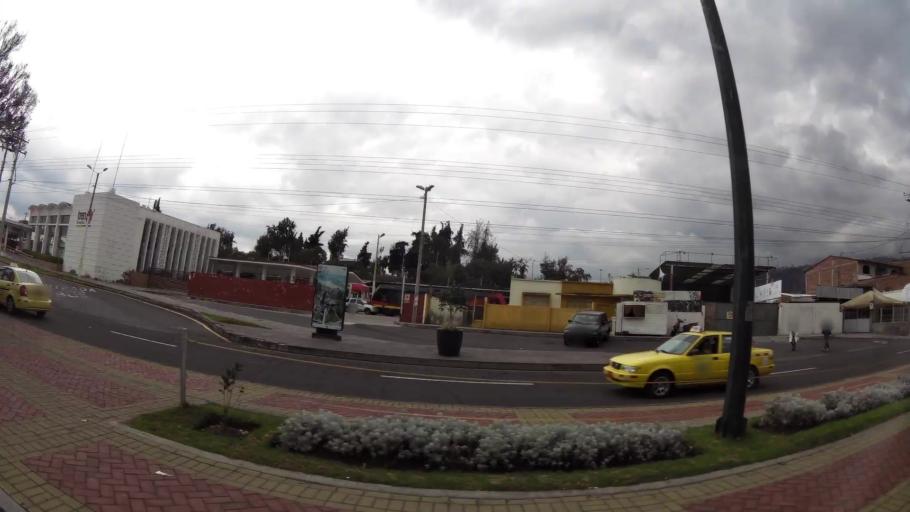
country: EC
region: Tungurahua
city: Ambato
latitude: -1.2343
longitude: -78.6172
